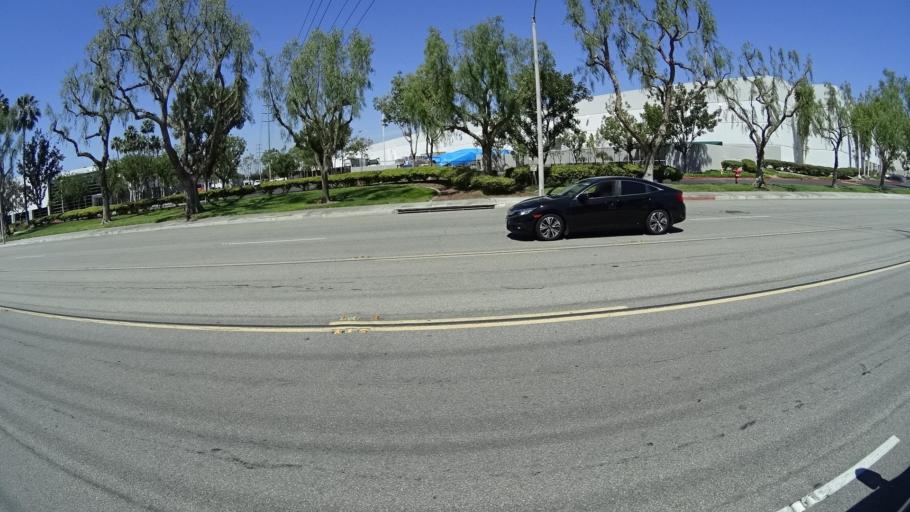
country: US
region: California
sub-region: Los Angeles County
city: Walnut
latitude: 34.0124
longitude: -117.8444
